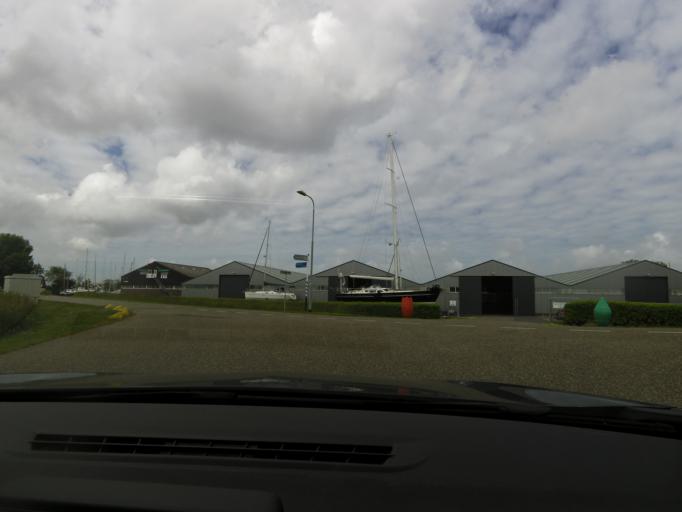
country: NL
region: Zeeland
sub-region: Schouwen-Duiveland
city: Scharendijke
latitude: 51.7296
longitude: 3.9112
